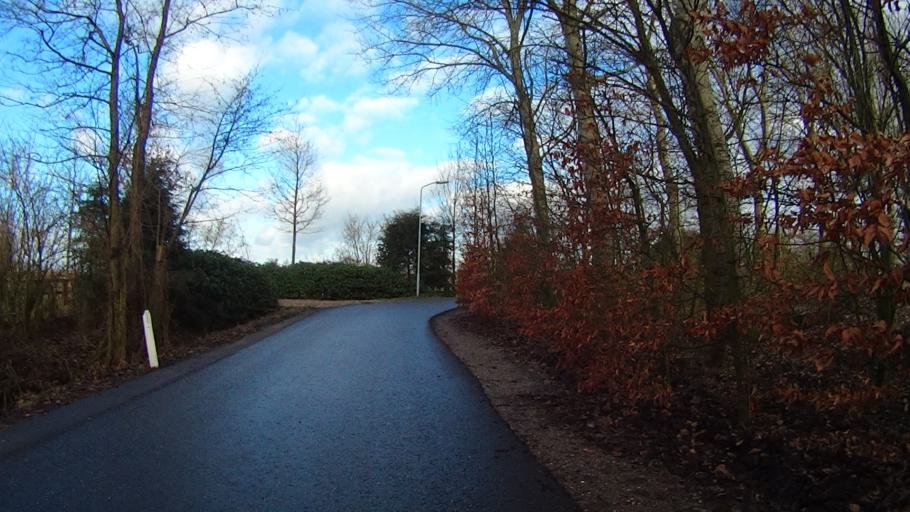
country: NL
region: Gelderland
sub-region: Gemeente Barneveld
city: Zwartebroek
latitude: 52.1687
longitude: 5.4789
